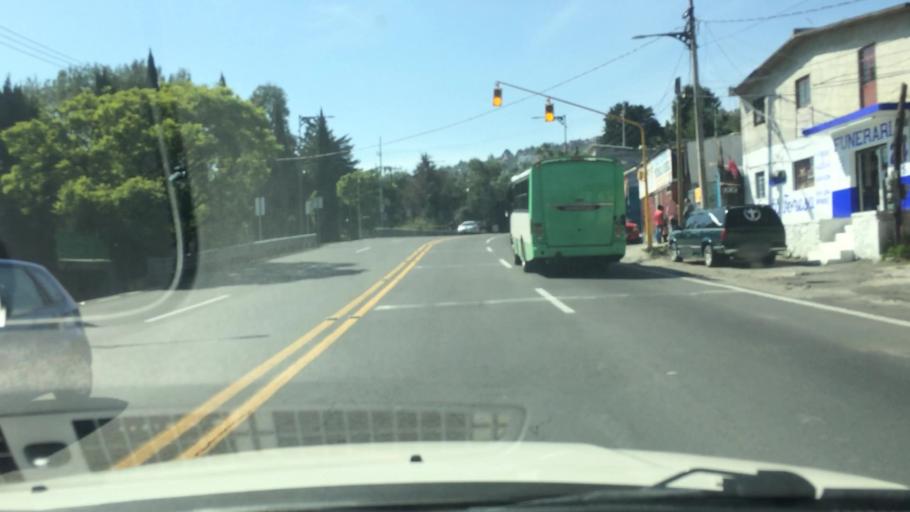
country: MX
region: Mexico City
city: Tlalpan
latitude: 19.2437
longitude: -99.1689
